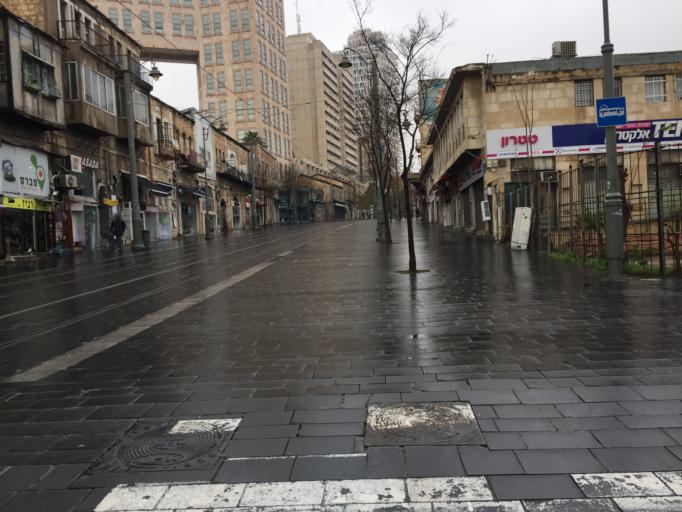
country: IL
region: Jerusalem
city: West Jerusalem
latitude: 31.7838
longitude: 35.2168
